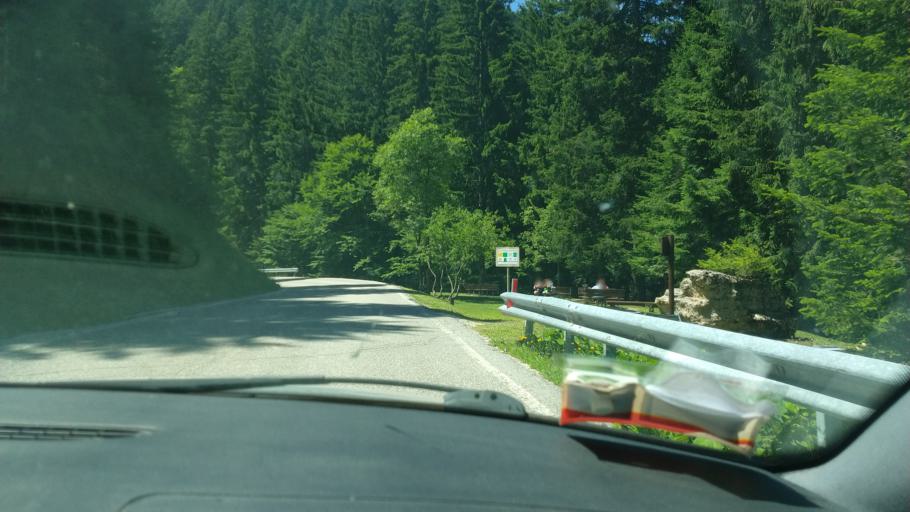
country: IT
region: Veneto
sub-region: Provincia di Vicenza
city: Lastebasse
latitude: 45.9056
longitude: 11.2225
